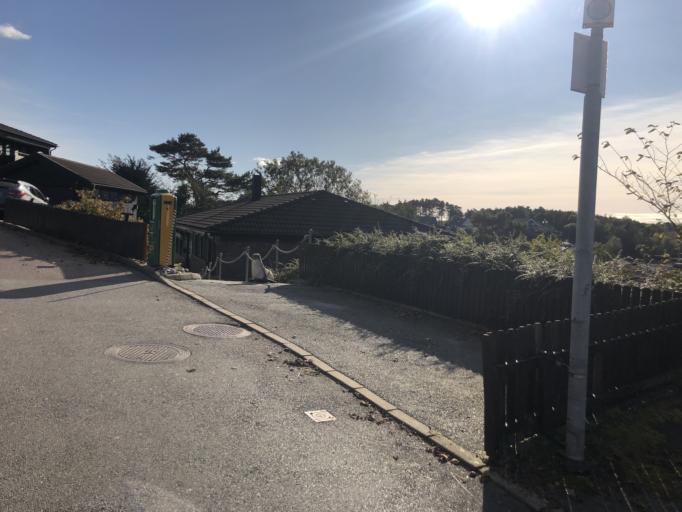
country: SE
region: Vaestra Goetaland
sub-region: Goteborg
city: Majorna
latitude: 57.6348
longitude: 11.9221
